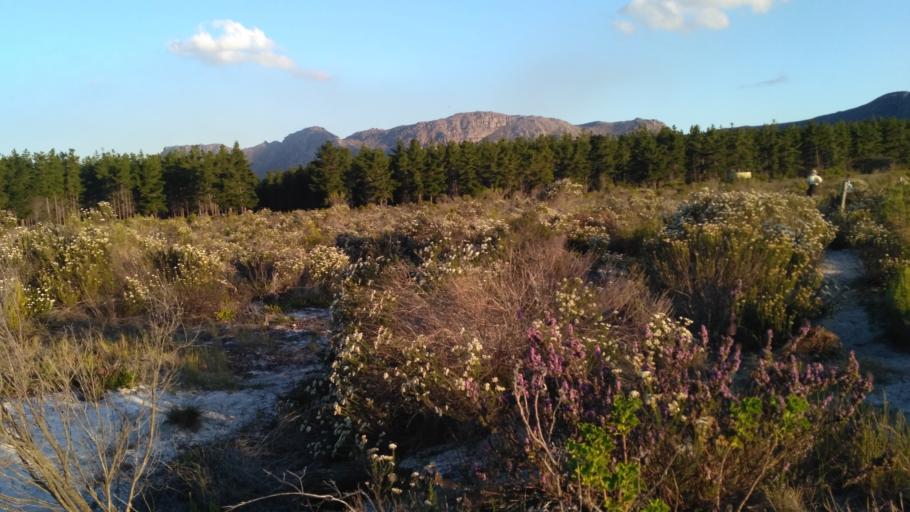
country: ZA
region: Western Cape
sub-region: City of Cape Town
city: Bergvliet
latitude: -34.0531
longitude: 18.4353
